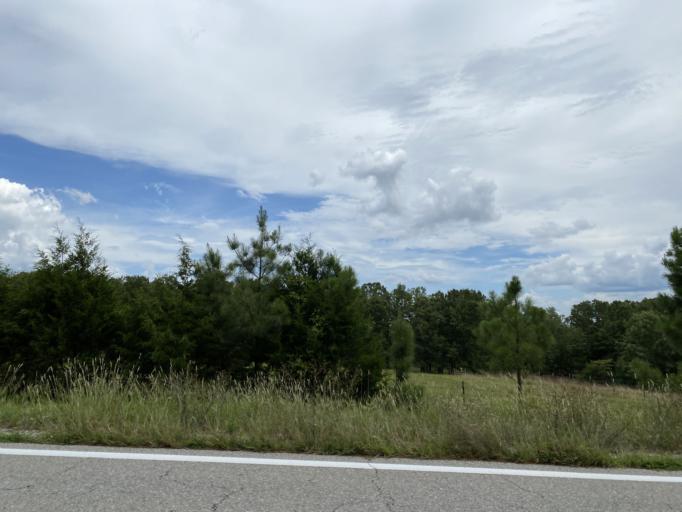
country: US
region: Arkansas
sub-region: Fulton County
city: Salem
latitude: 36.4252
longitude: -91.7083
